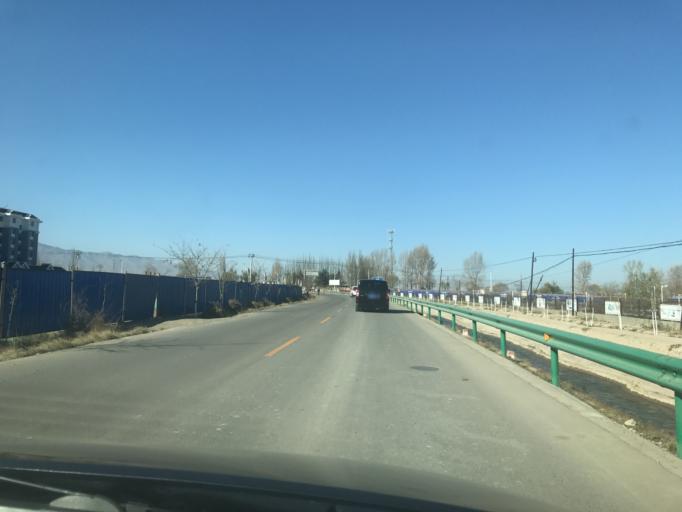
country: CN
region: Gansu Sheng
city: Gulang
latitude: 37.6769
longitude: 102.8375
